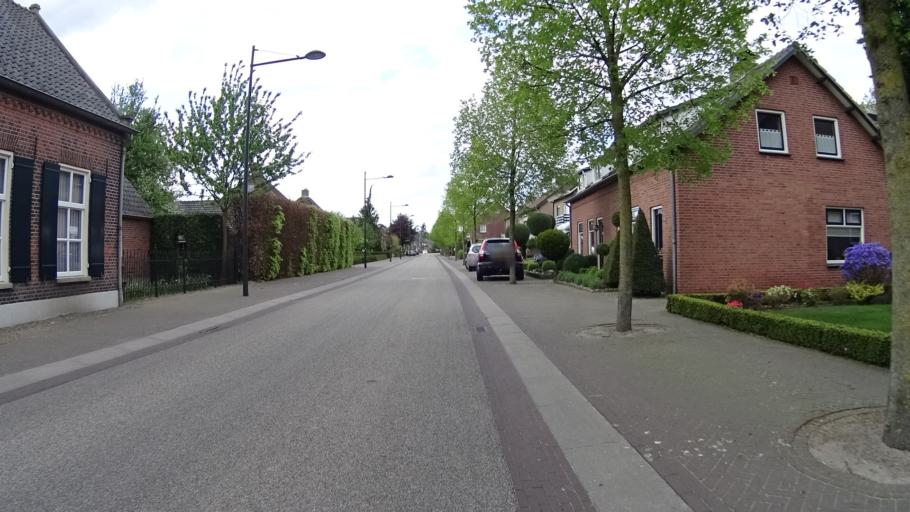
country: NL
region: North Brabant
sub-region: Gemeente Boekel
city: Boekel
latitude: 51.5818
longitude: 5.7117
